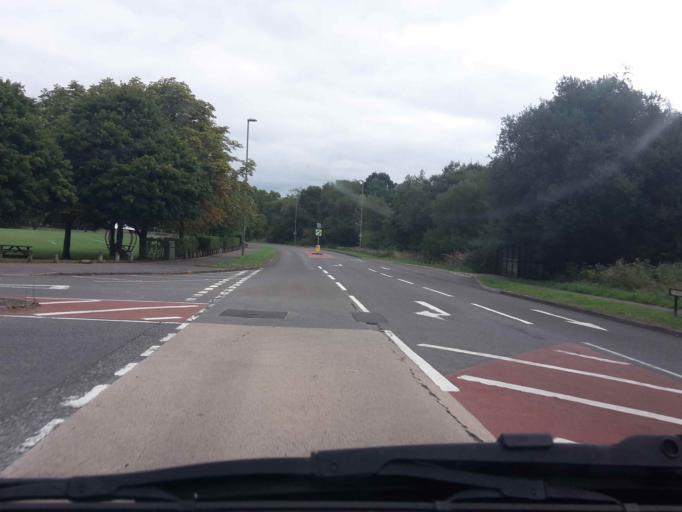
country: GB
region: England
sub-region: Hampshire
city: Fleet
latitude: 51.2942
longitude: -0.8225
